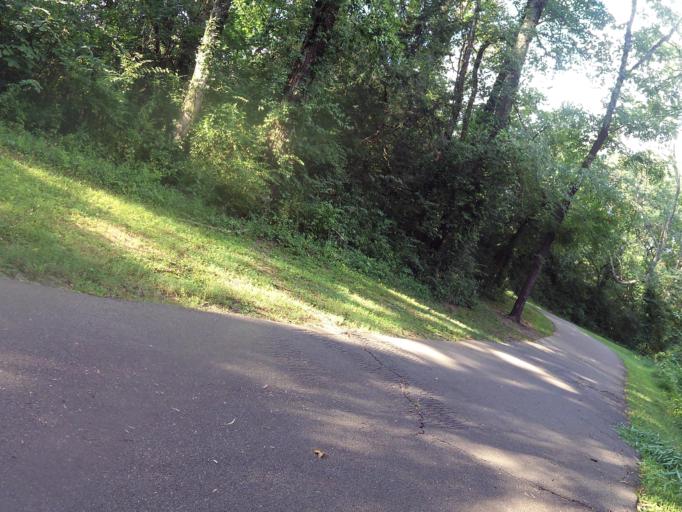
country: US
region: Tennessee
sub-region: Knox County
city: Knoxville
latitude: 35.9516
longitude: -83.9587
